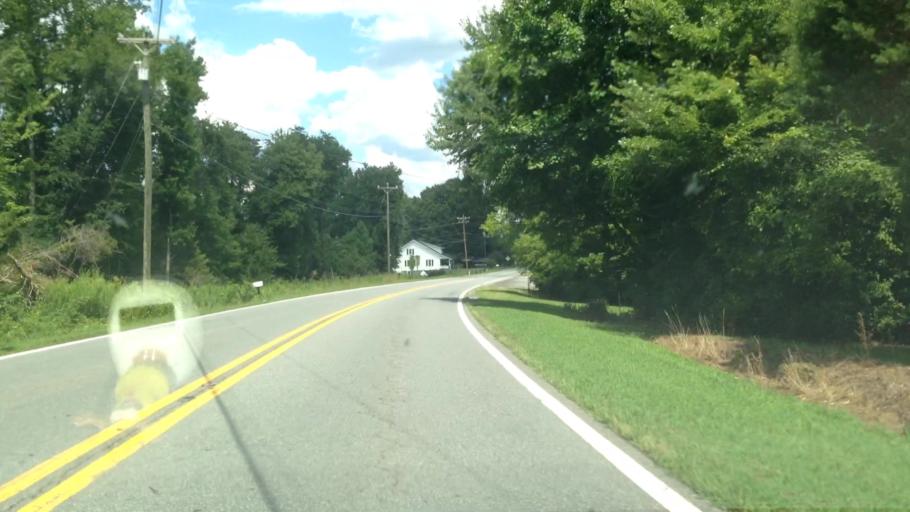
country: US
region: North Carolina
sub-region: Rockingham County
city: Reidsville
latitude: 36.4010
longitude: -79.6285
